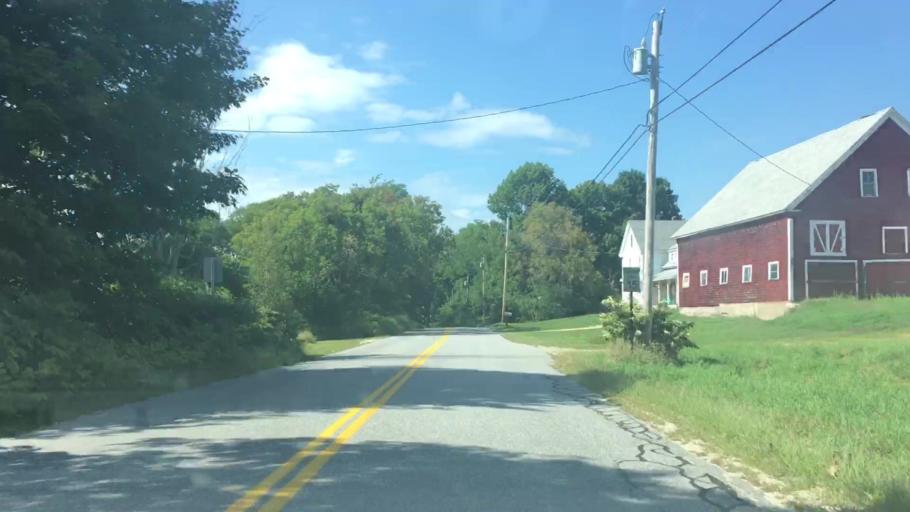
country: US
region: Maine
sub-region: Androscoggin County
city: Poland
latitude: 44.0063
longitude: -70.3739
